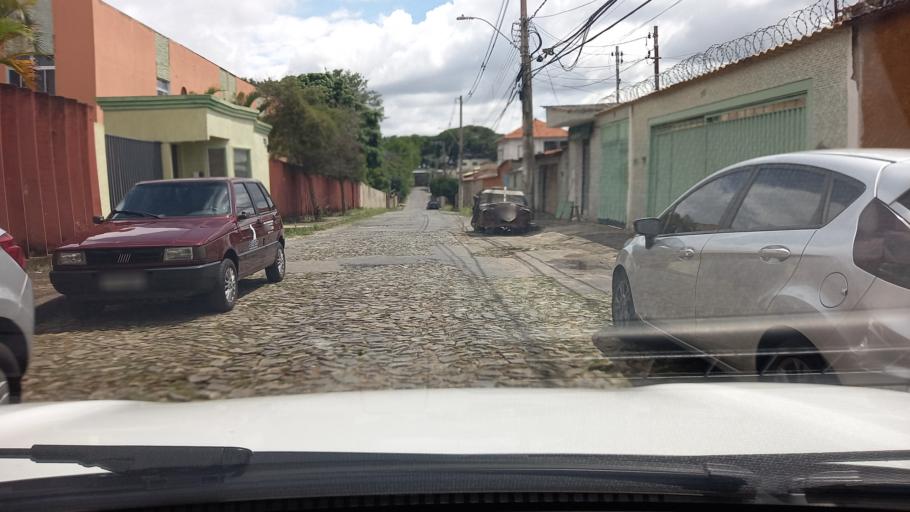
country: BR
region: Minas Gerais
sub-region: Contagem
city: Contagem
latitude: -19.8999
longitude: -44.0238
